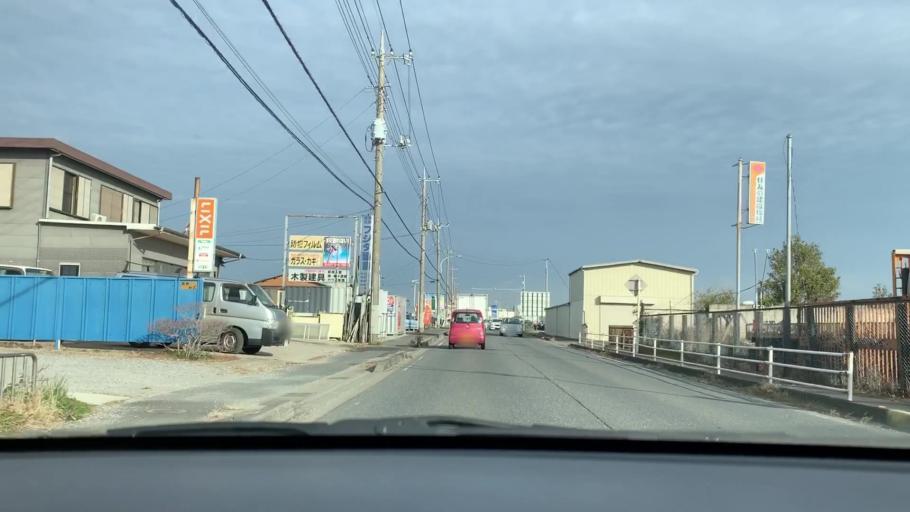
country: JP
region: Chiba
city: Nagareyama
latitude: 35.8201
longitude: 139.8955
